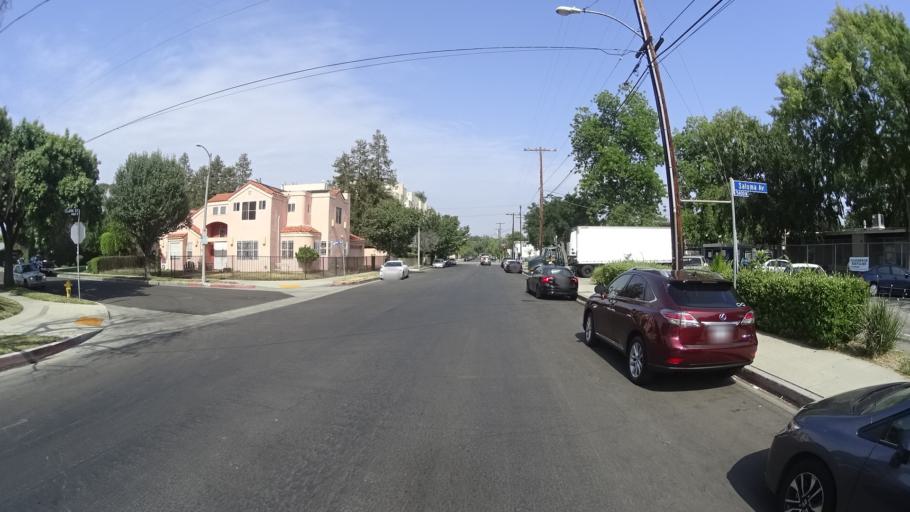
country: US
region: California
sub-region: Los Angeles County
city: Sherman Oaks
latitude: 34.1685
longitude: -118.4587
